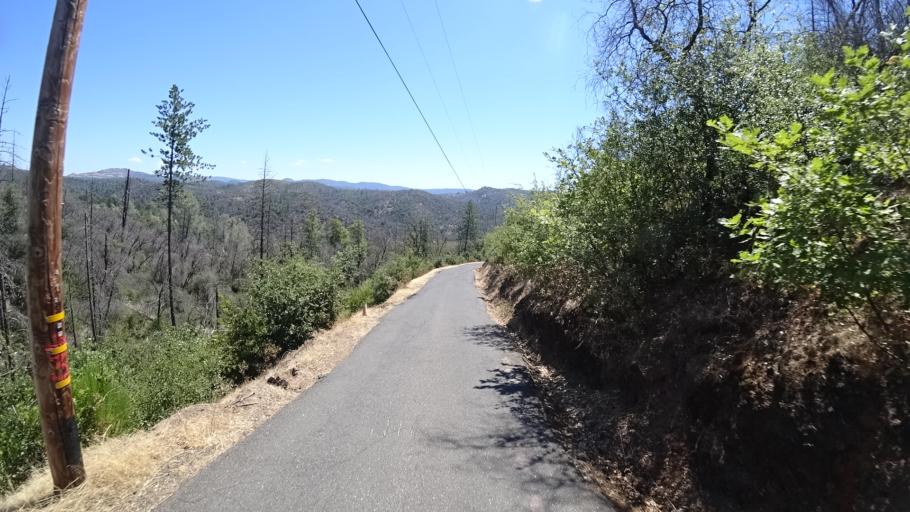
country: US
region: California
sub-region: Calaveras County
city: Mountain Ranch
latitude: 38.2062
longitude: -120.5176
